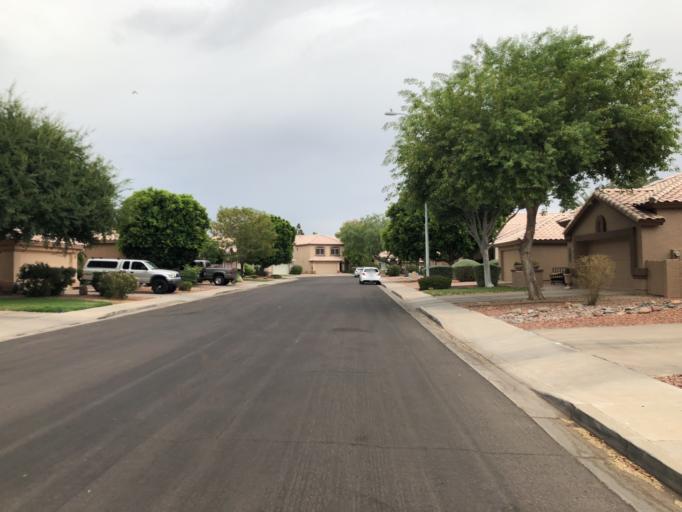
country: US
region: Arizona
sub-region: Maricopa County
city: Guadalupe
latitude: 33.3181
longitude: -111.9319
